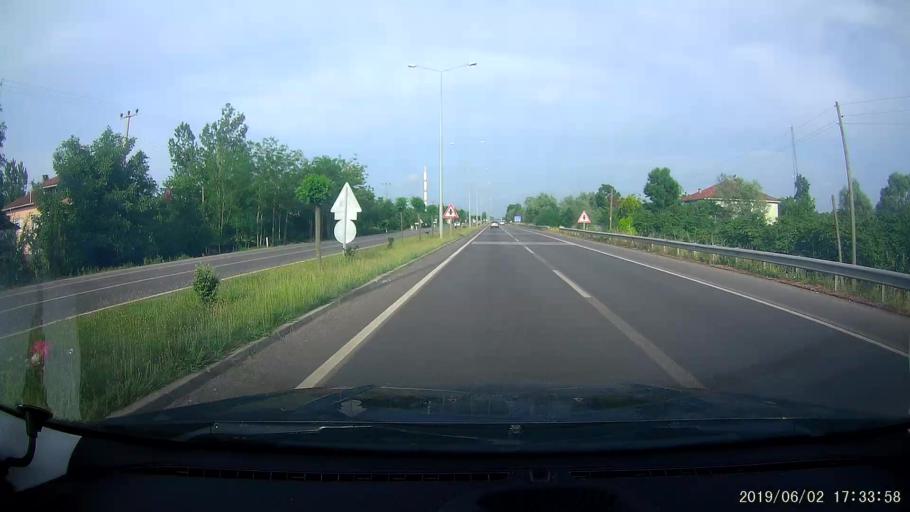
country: TR
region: Samsun
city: Terme
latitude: 41.2206
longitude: 36.8597
